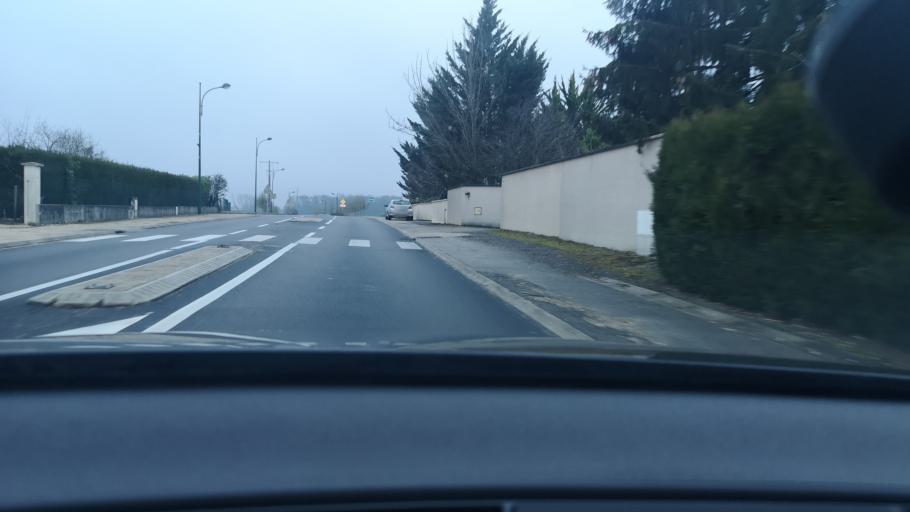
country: FR
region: Bourgogne
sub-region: Departement de la Cote-d'Or
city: Fenay
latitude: 47.1894
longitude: 5.0791
